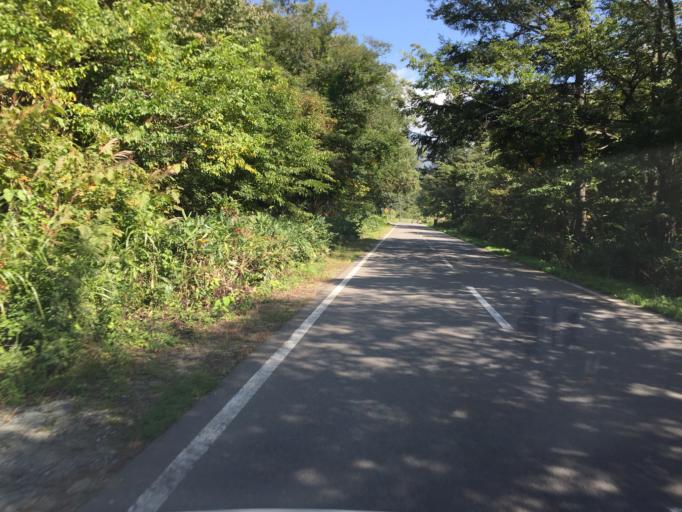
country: JP
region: Fukushima
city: Inawashiro
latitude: 37.6545
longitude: 140.1906
